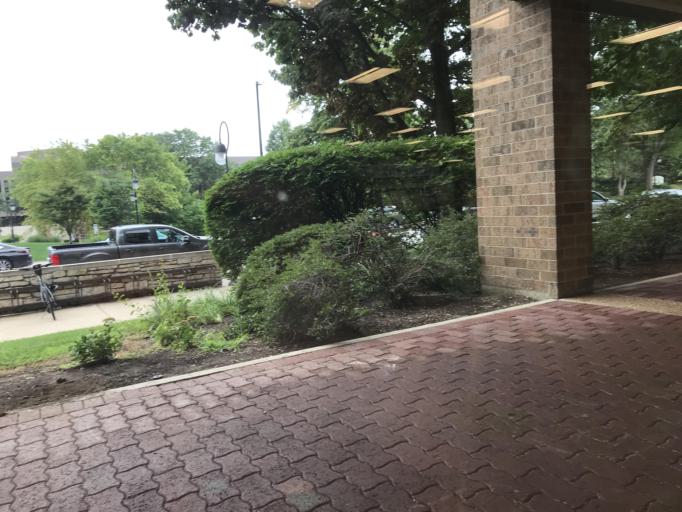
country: US
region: Illinois
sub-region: DuPage County
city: Naperville
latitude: 41.7720
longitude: -88.1519
